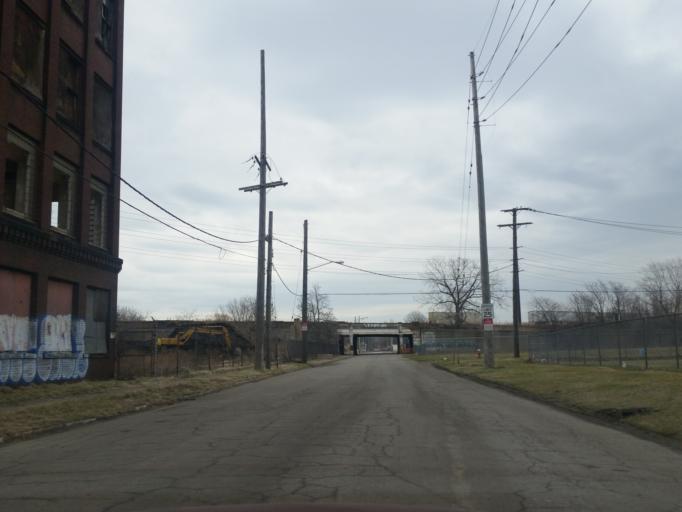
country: US
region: Ohio
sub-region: Cuyahoga County
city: Newburgh Heights
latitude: 41.4904
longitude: -81.6383
